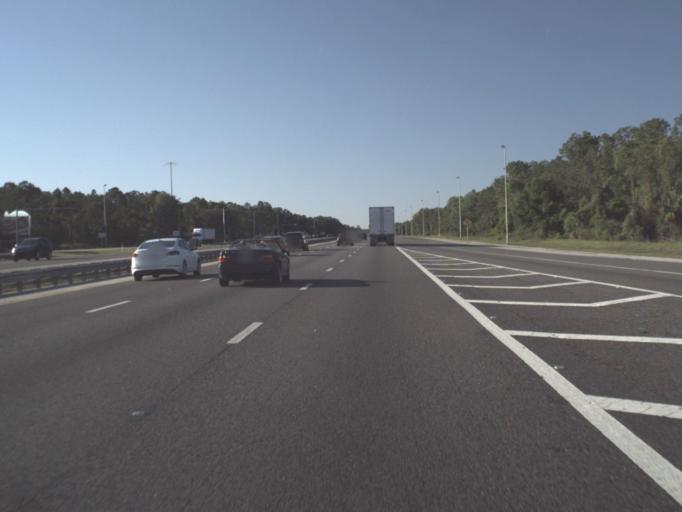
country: US
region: Florida
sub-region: Flagler County
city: Palm Coast
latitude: 29.5136
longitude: -81.1980
